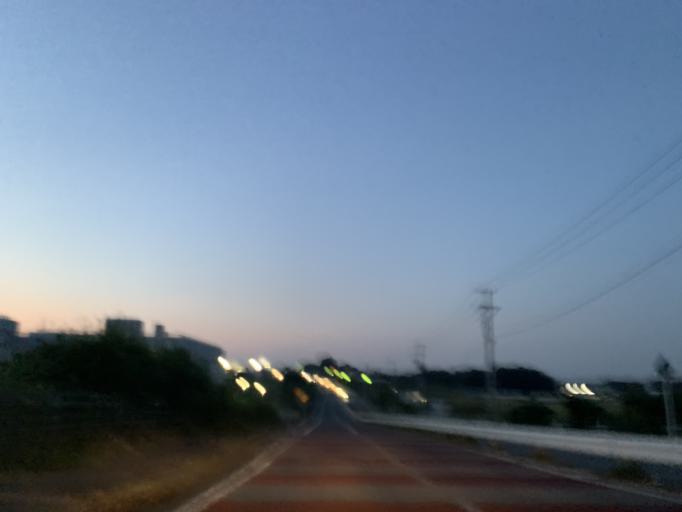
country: JP
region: Chiba
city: Nagareyama
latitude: 35.8726
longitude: 139.9077
